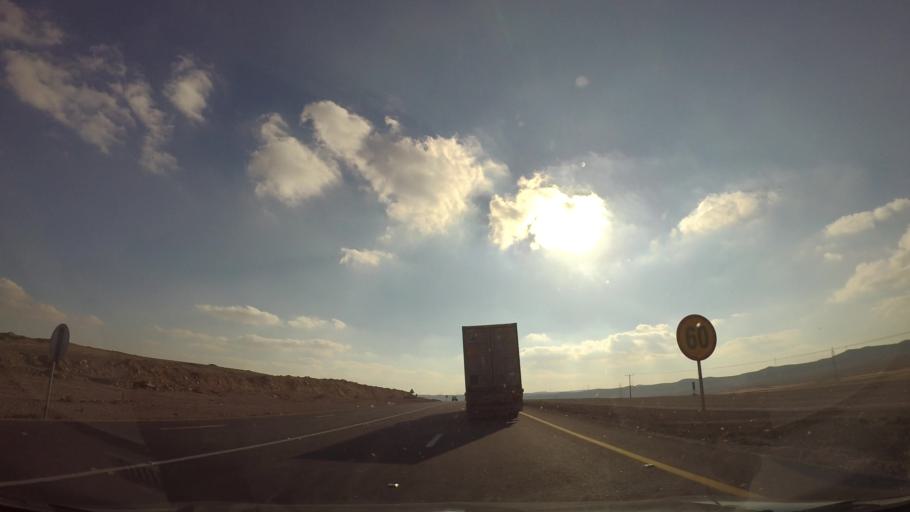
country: JO
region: Karak
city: Karak City
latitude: 31.1277
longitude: 36.0204
